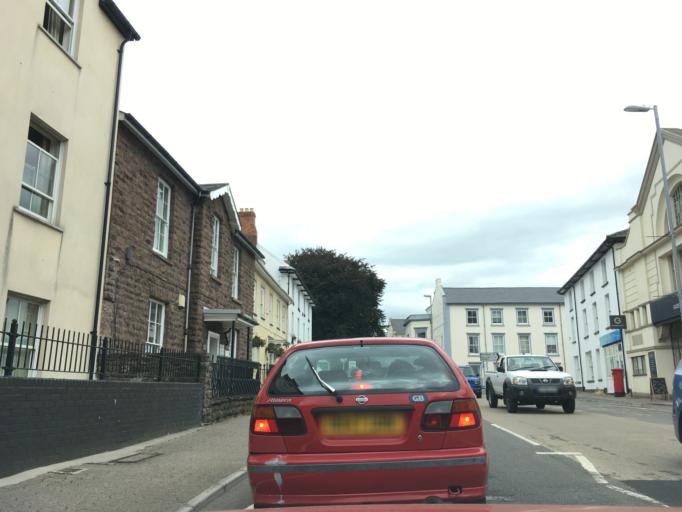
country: GB
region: Wales
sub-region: Monmouthshire
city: Abergavenny
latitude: 51.8221
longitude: -3.0158
